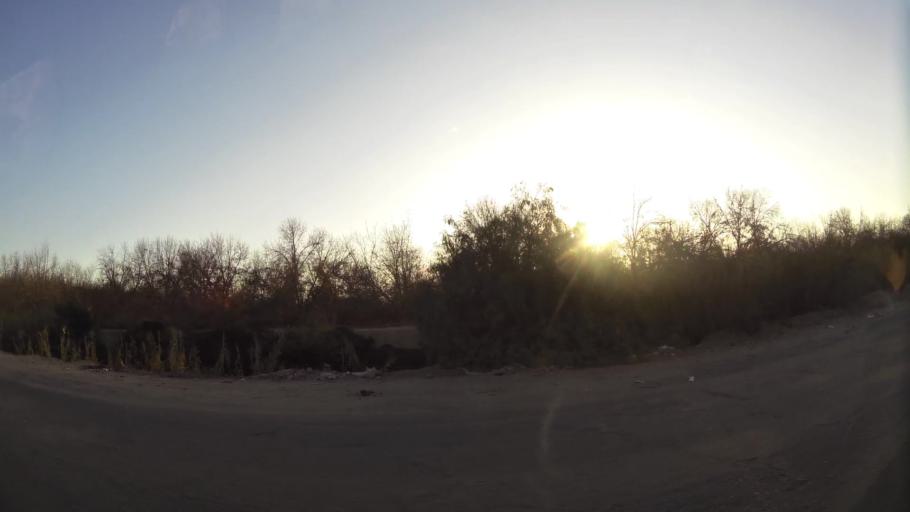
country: PE
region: Ica
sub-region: Provincia de Ica
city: Ica
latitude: -14.0848
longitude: -75.7174
